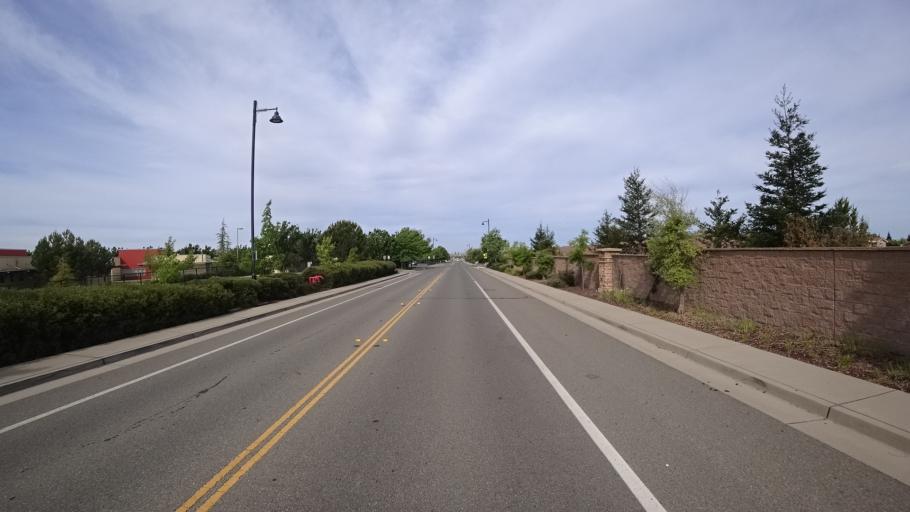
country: US
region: California
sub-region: Placer County
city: Lincoln
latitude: 38.8375
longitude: -121.2867
